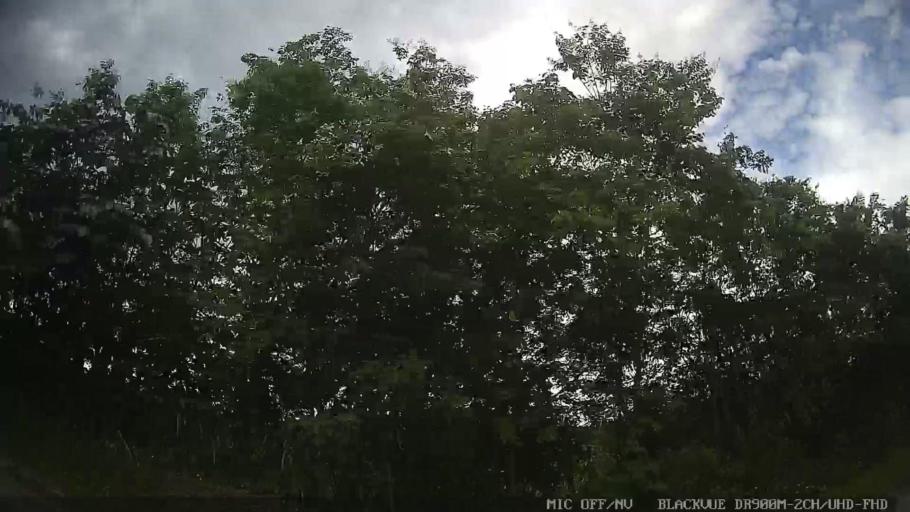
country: BR
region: Sao Paulo
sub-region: Biritiba-Mirim
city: Biritiba Mirim
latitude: -23.5522
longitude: -45.9717
